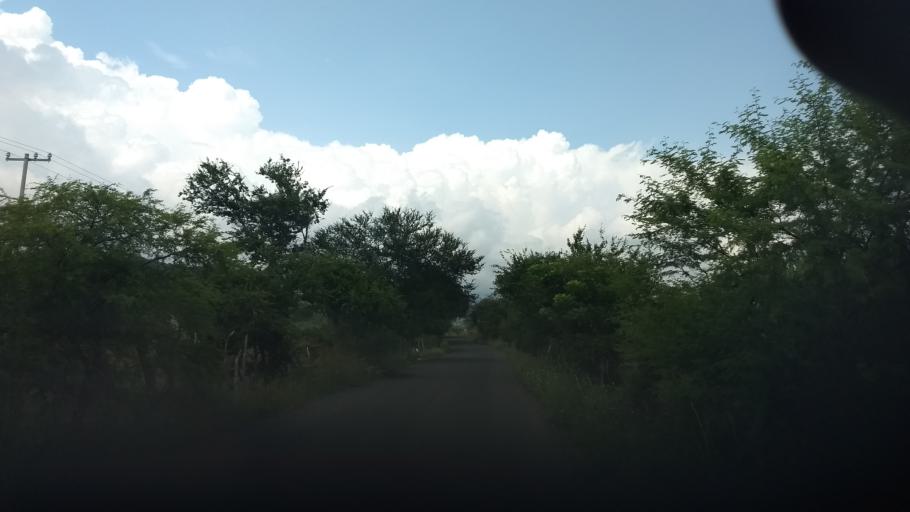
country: MX
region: Jalisco
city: Tonila
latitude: 19.4116
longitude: -103.4868
